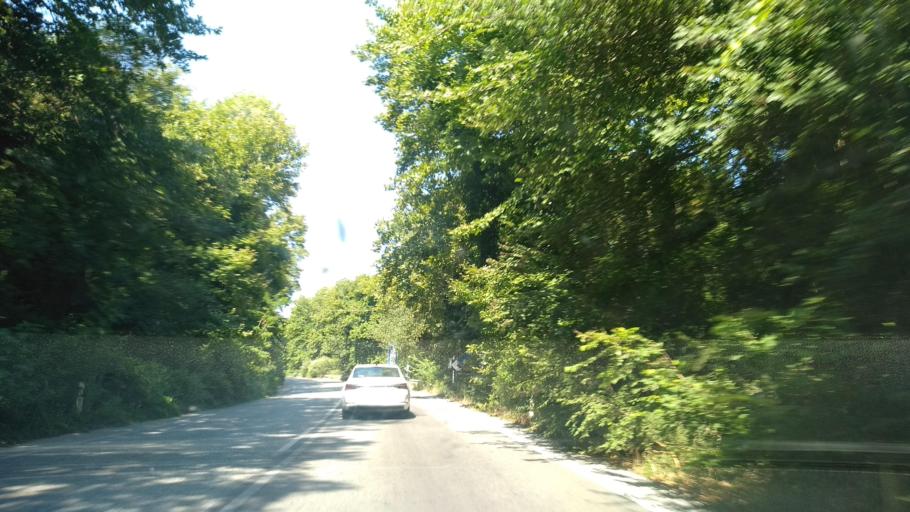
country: GR
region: Central Macedonia
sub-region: Nomos Thessalonikis
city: Stavros
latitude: 40.6584
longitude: 23.6195
